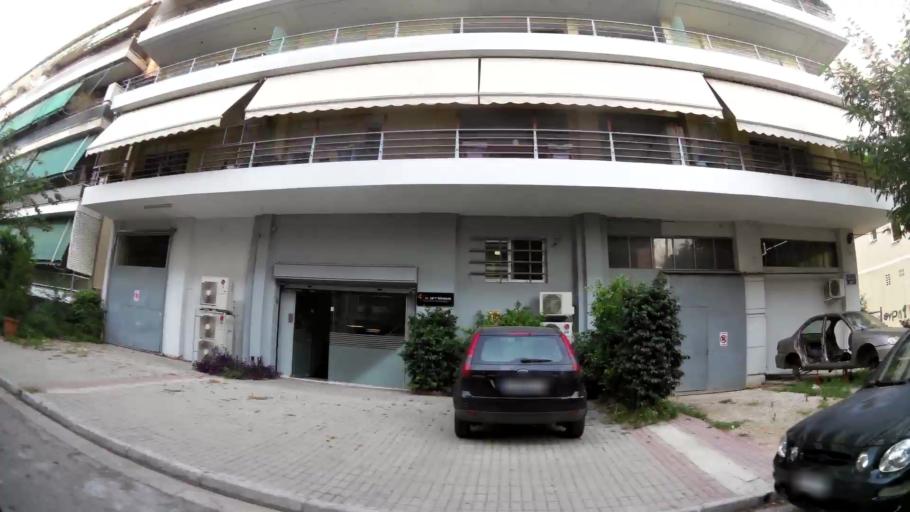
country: GR
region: Attica
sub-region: Nomarchia Athinas
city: Kallithea
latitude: 37.9512
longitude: 23.6901
